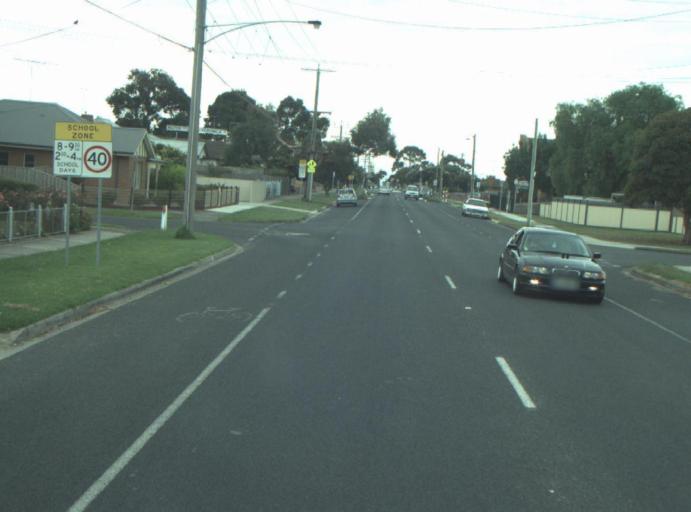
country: AU
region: Victoria
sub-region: Greater Geelong
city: East Geelong
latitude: -38.1677
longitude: 144.3920
